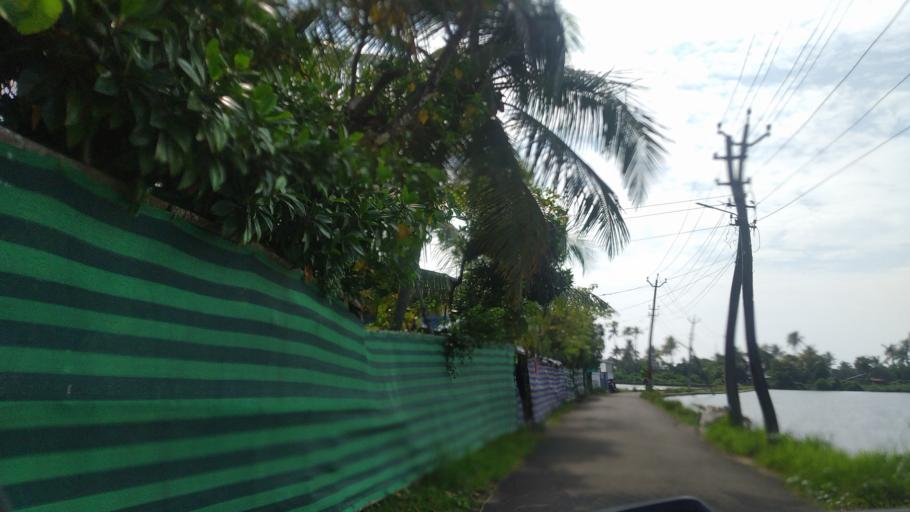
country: IN
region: Kerala
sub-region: Ernakulam
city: Elur
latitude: 10.0823
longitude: 76.1995
